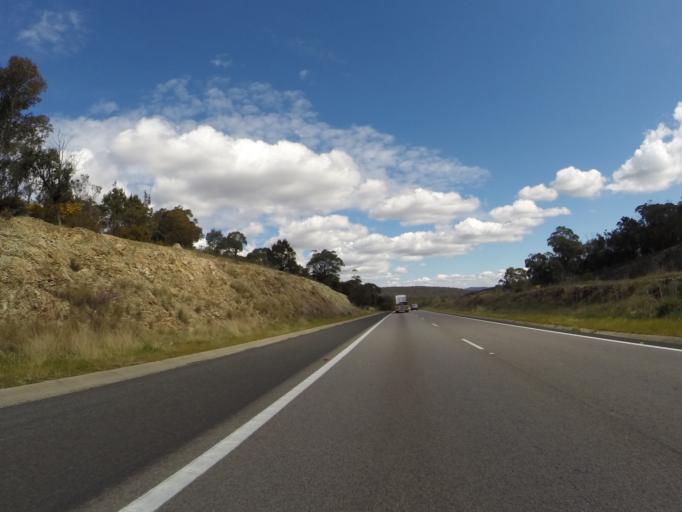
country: AU
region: New South Wales
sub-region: Goulburn Mulwaree
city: Goulburn
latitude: -34.7407
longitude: 149.9417
